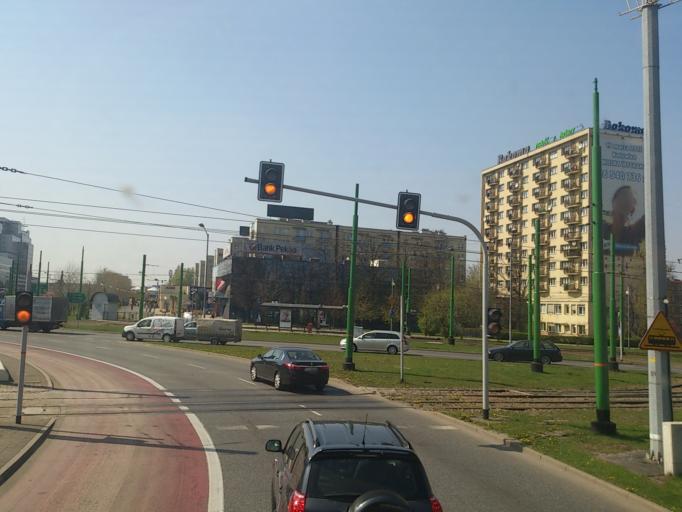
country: PL
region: Silesian Voivodeship
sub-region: Katowice
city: Katowice
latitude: 50.2647
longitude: 19.0240
